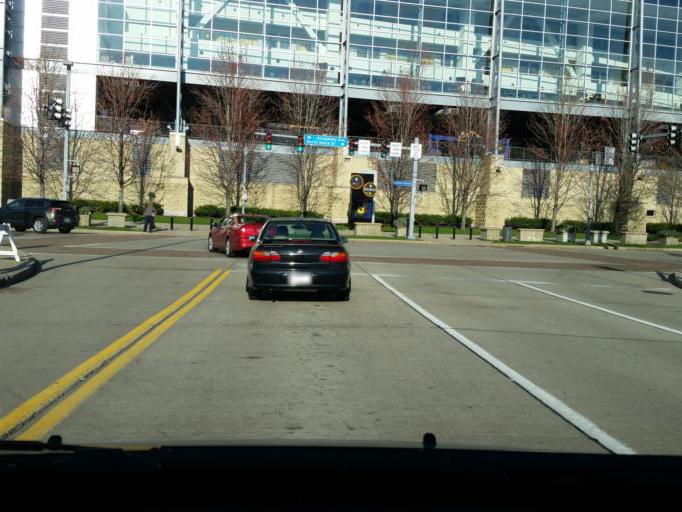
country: US
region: Pennsylvania
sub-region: Allegheny County
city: Pittsburgh
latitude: 40.4468
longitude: -80.0179
